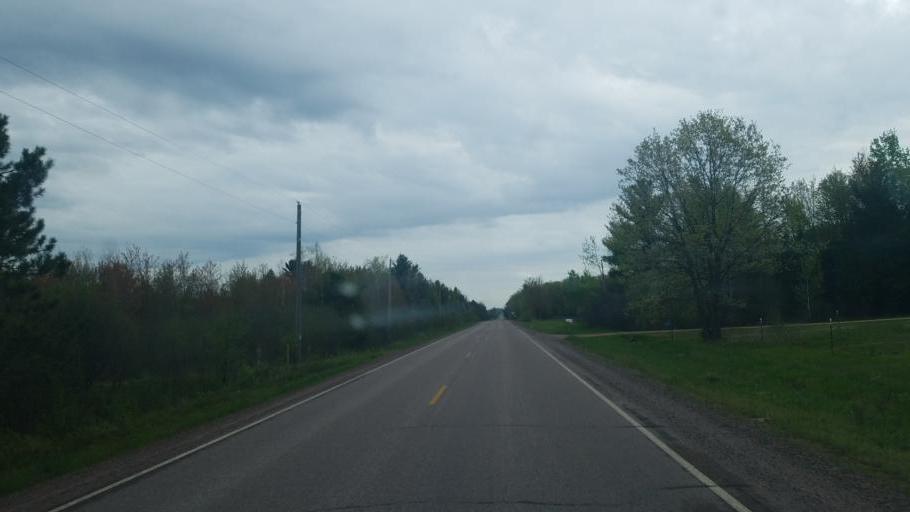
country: US
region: Wisconsin
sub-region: Wood County
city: Marshfield
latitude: 44.5591
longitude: -90.3000
